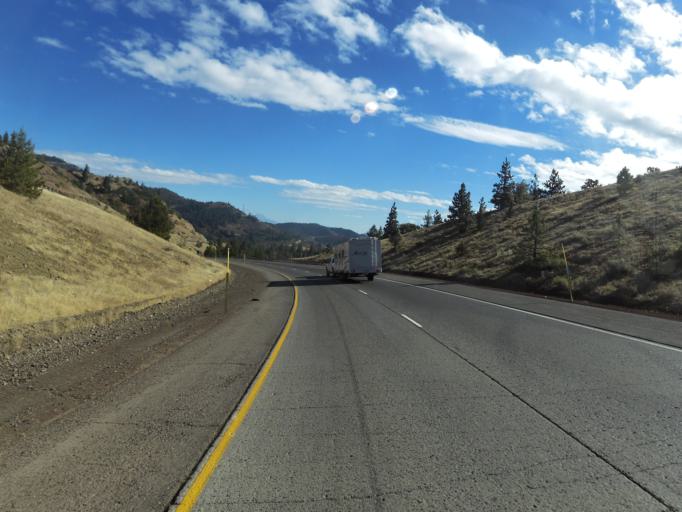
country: US
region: Oregon
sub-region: Jackson County
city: Ashland
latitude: 42.0531
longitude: -122.6104
